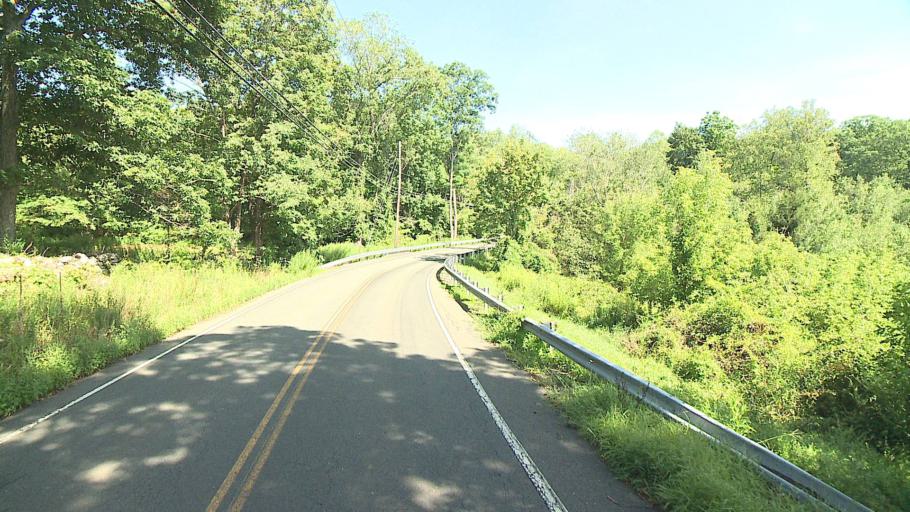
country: US
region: Connecticut
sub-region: Hartford County
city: West Simsbury
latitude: 41.8934
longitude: -72.8846
